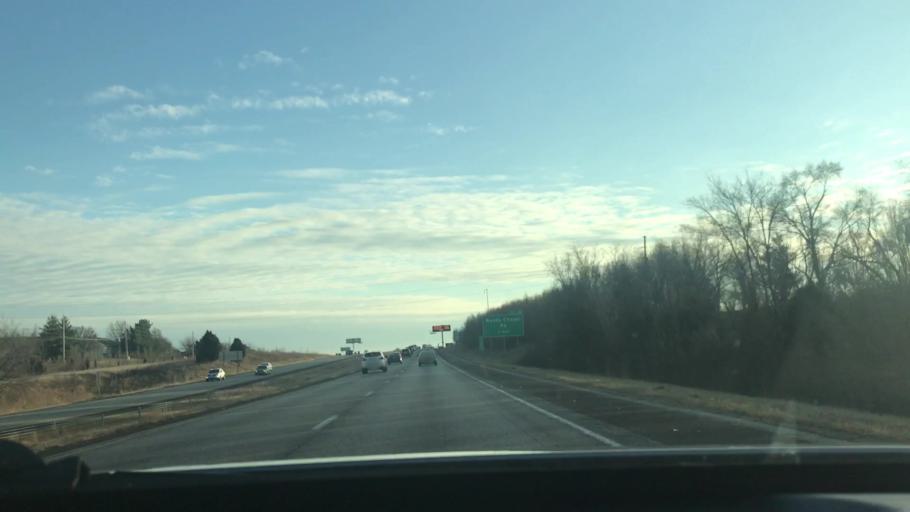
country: US
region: Missouri
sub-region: Jackson County
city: Blue Springs
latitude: 38.9980
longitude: -94.3574
